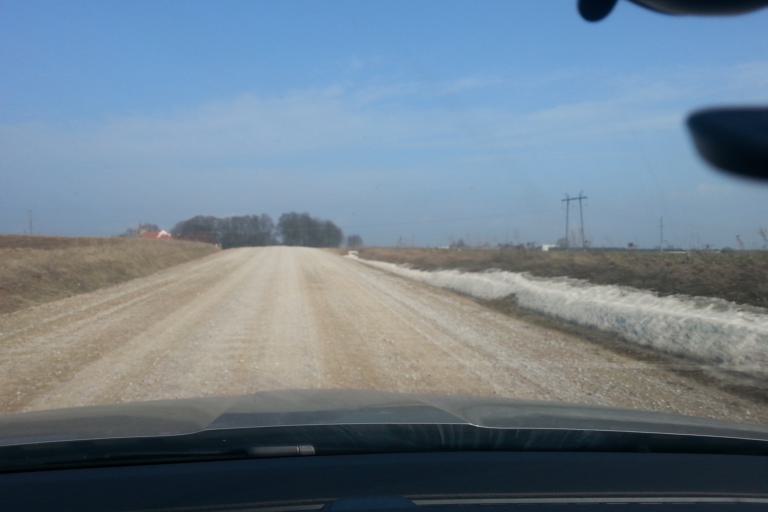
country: LT
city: Trakai
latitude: 54.6015
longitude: 24.9820
